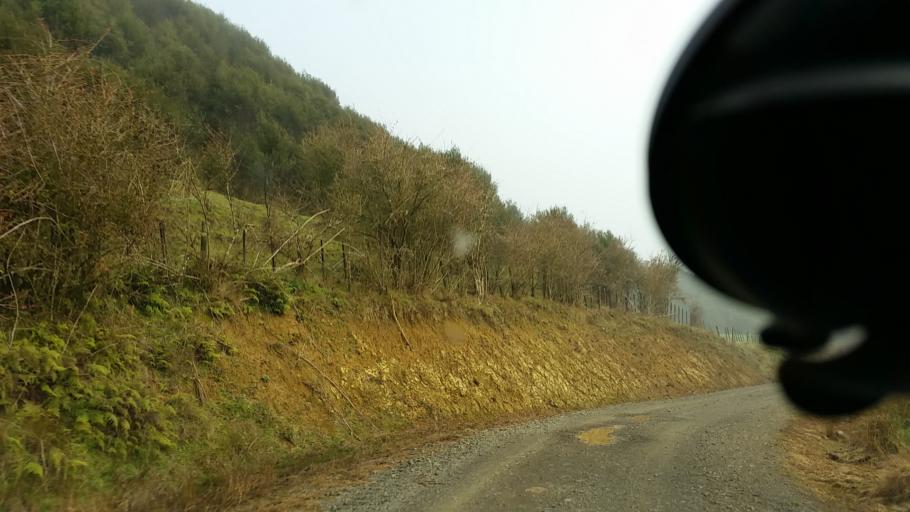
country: NZ
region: Taranaki
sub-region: New Plymouth District
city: Waitara
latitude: -38.9736
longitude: 174.8052
